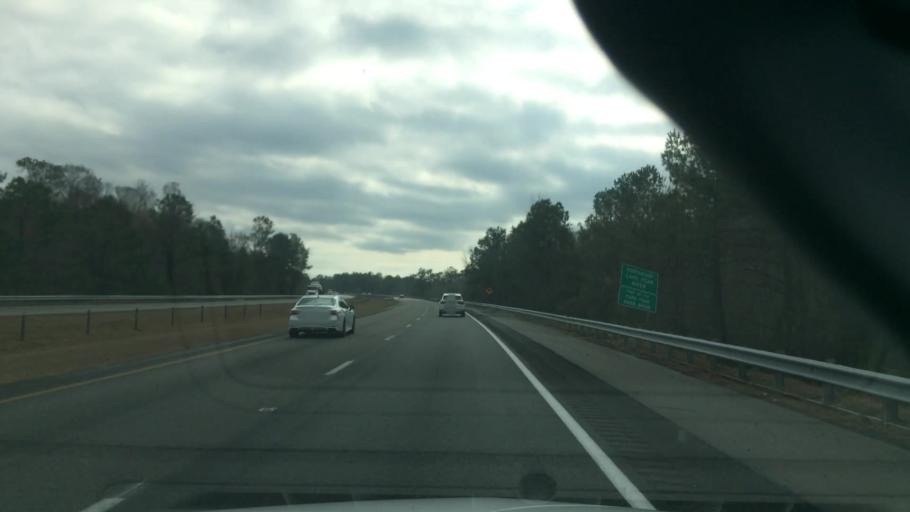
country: US
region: North Carolina
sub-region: New Hanover County
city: Castle Hayne
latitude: 34.3684
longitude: -77.8879
